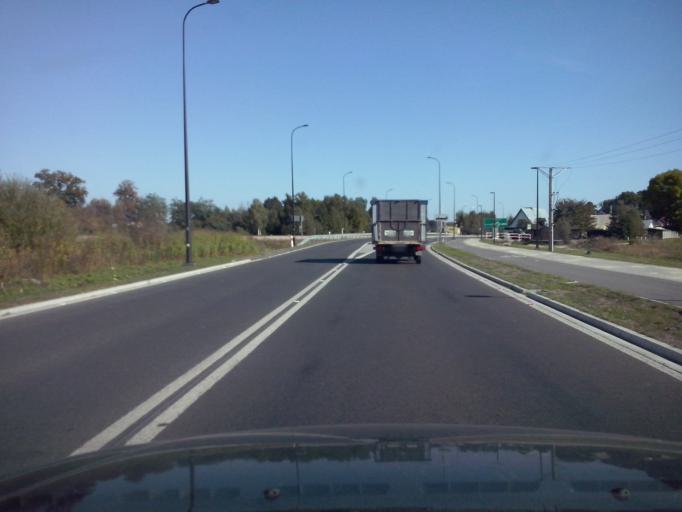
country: PL
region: Lublin Voivodeship
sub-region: Powiat bilgorajski
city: Bilgoraj
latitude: 50.5493
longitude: 22.7204
